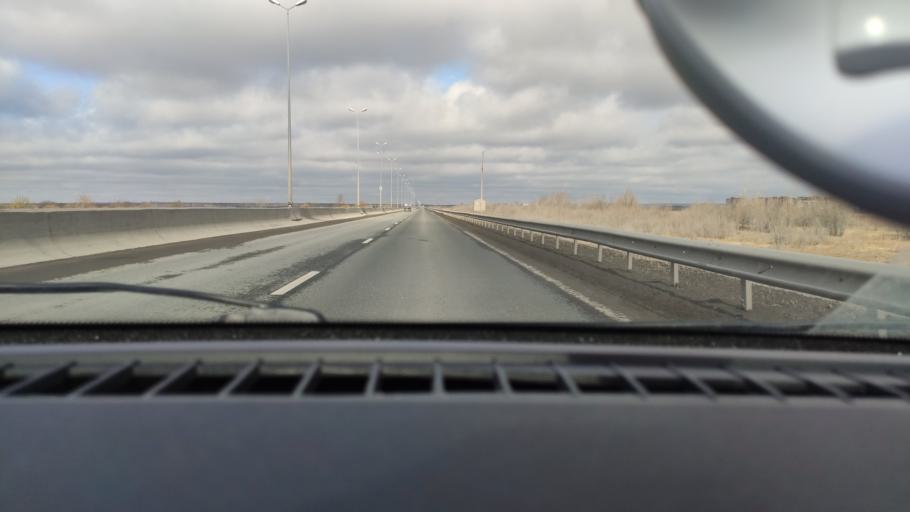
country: RU
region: Perm
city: Kondratovo
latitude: 57.9627
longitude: 56.1070
